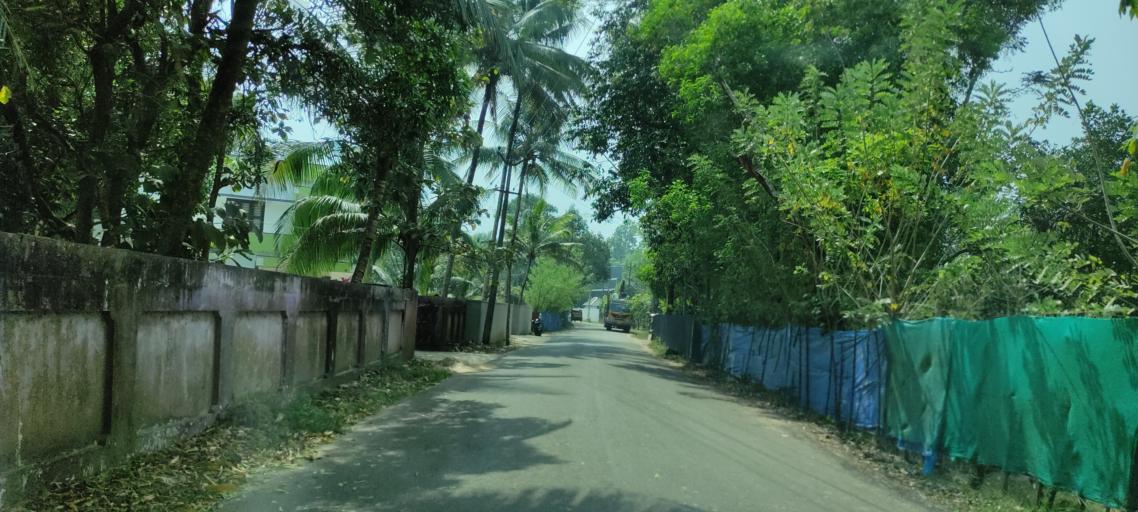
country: IN
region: Kerala
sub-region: Alappuzha
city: Shertallai
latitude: 9.6299
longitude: 76.3516
